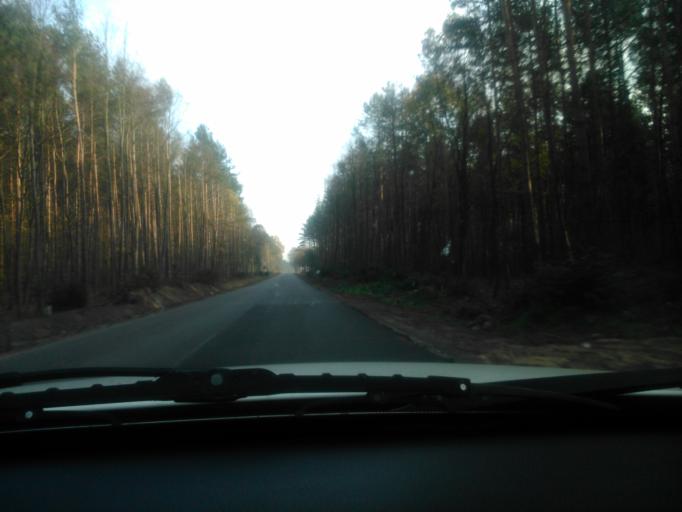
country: PL
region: Warmian-Masurian Voivodeship
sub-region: Powiat dzialdowski
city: Lidzbark
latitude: 53.2567
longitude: 19.8860
